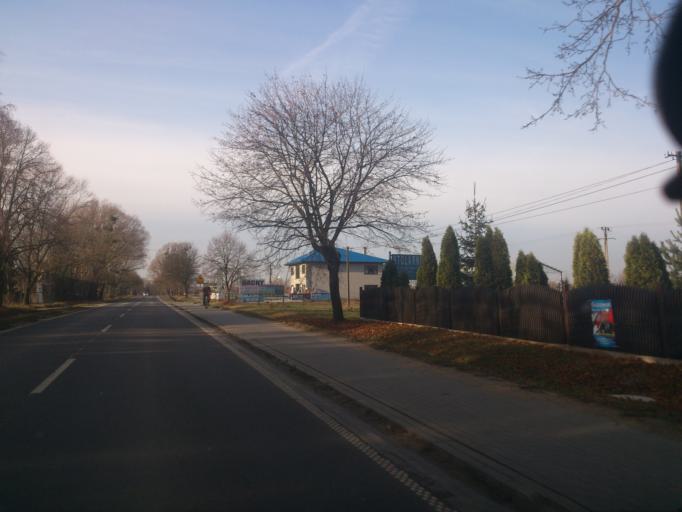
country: PL
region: Kujawsko-Pomorskie
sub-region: Powiat golubsko-dobrzynski
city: Golub-Dobrzyn
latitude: 53.1090
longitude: 19.0879
